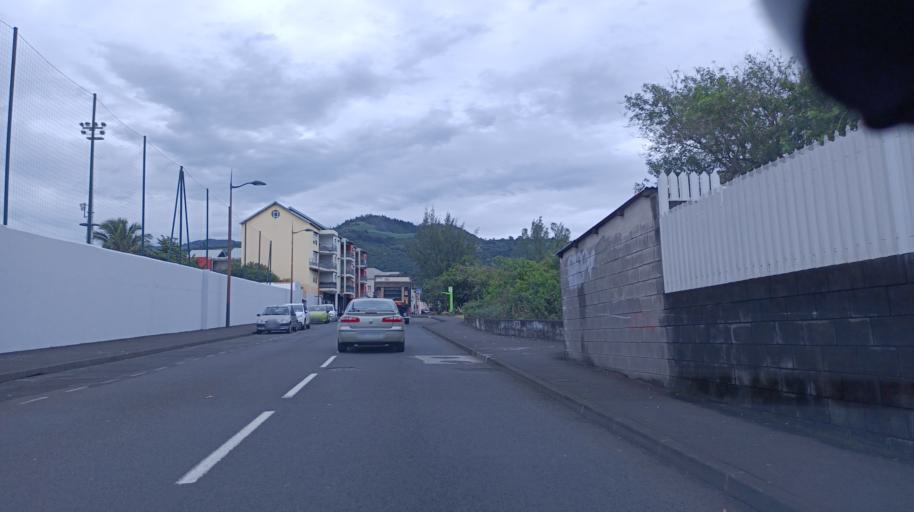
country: RE
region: Reunion
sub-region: Reunion
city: Saint-Joseph
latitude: -21.3787
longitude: 55.6154
